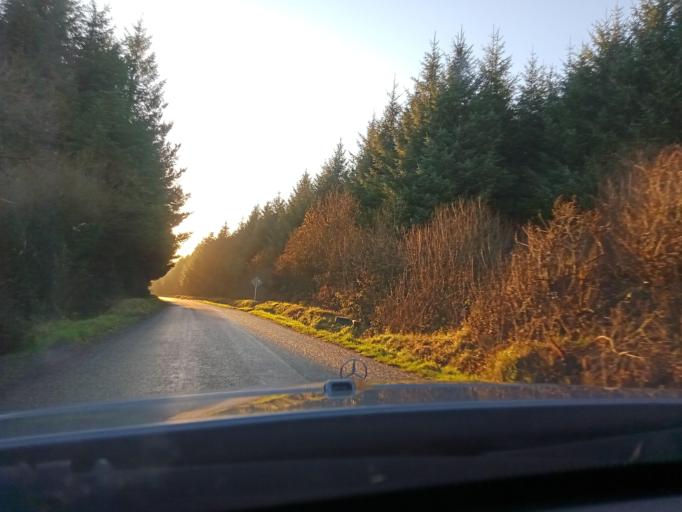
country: IE
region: Munster
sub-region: Waterford
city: Waterford
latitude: 52.3732
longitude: -7.1022
